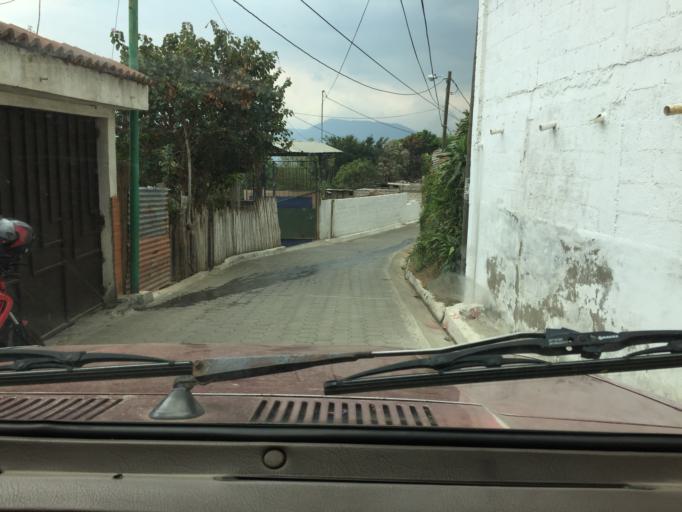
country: GT
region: Guatemala
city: Amatitlan
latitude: 14.4927
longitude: -90.6417
